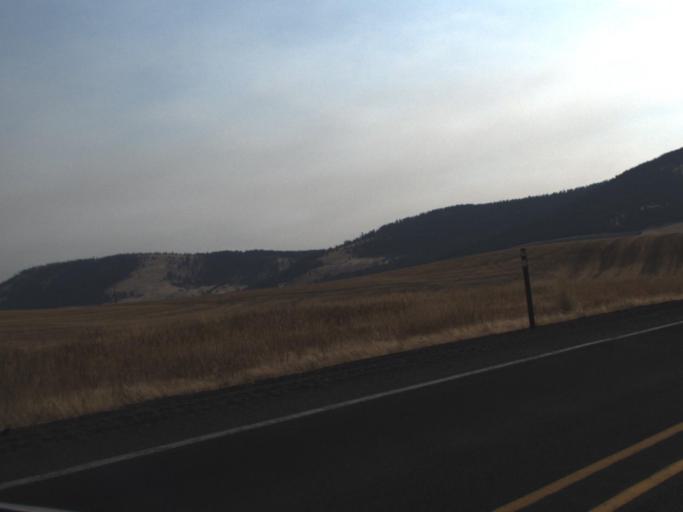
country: US
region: Idaho
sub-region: Benewah County
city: Plummer
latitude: 47.2746
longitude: -117.1333
